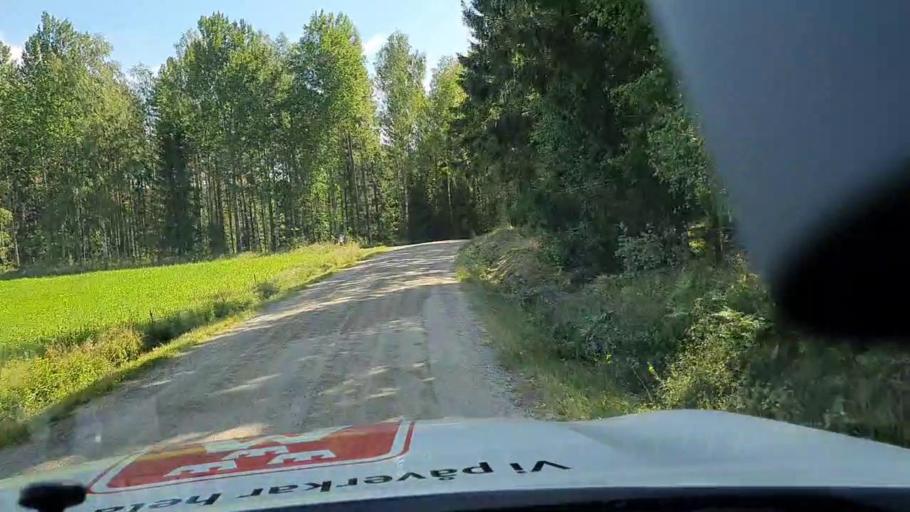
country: SE
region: Soedermanland
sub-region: Strangnas Kommun
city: Akers Styckebruk
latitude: 59.2020
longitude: 16.9181
